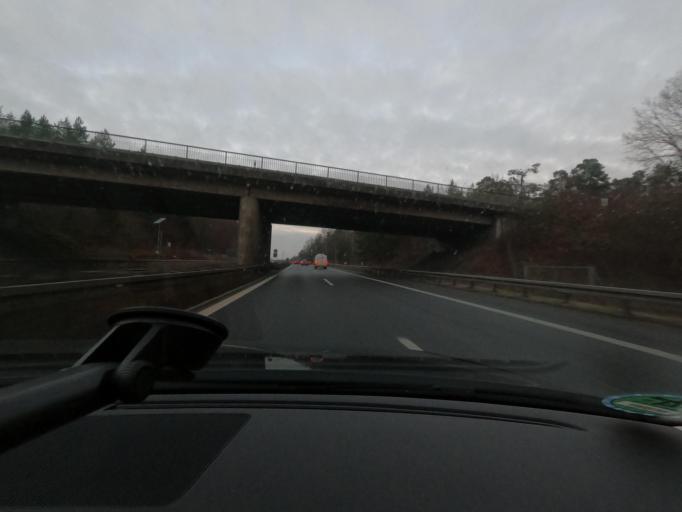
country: DE
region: Bavaria
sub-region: Upper Franconia
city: Memmelsdorf
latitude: 49.8885
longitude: 10.9495
